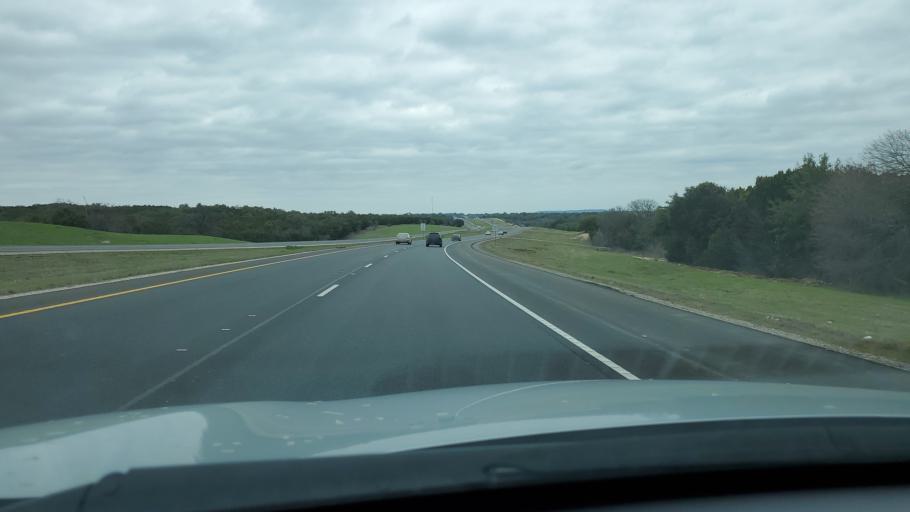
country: US
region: Texas
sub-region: Williamson County
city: Florence
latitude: 30.9061
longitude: -97.8007
